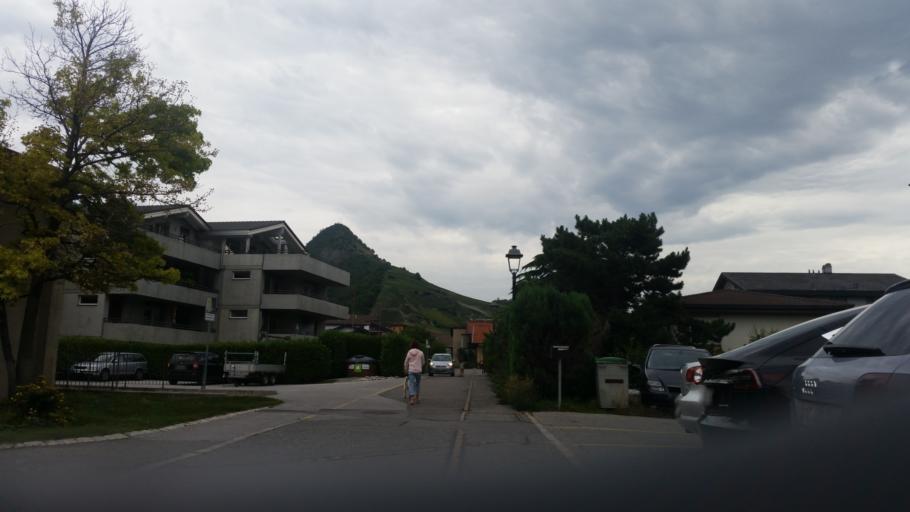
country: CH
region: Valais
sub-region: Conthey District
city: Conthey
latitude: 46.2314
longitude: 7.3063
